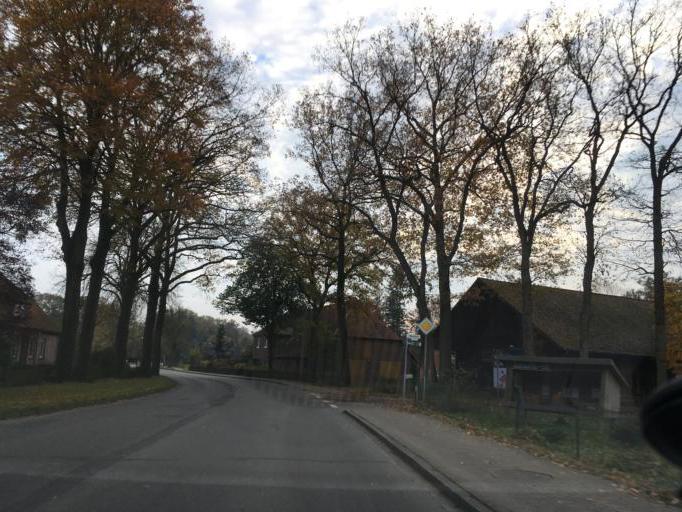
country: DE
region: Lower Saxony
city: Wietzendorf
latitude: 52.9459
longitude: 9.9814
